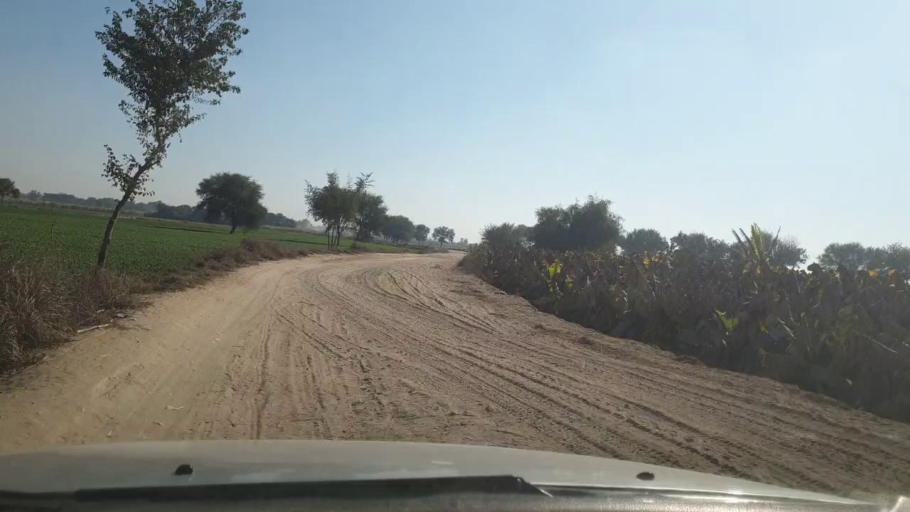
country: PK
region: Sindh
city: Ghotki
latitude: 28.0218
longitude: 69.2222
